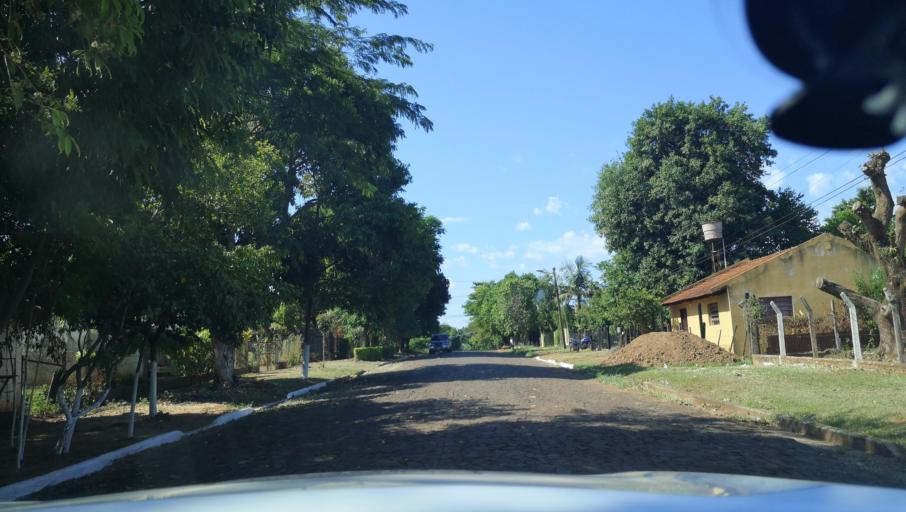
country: PY
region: Itapua
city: Carmen del Parana
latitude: -27.1621
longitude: -56.2341
